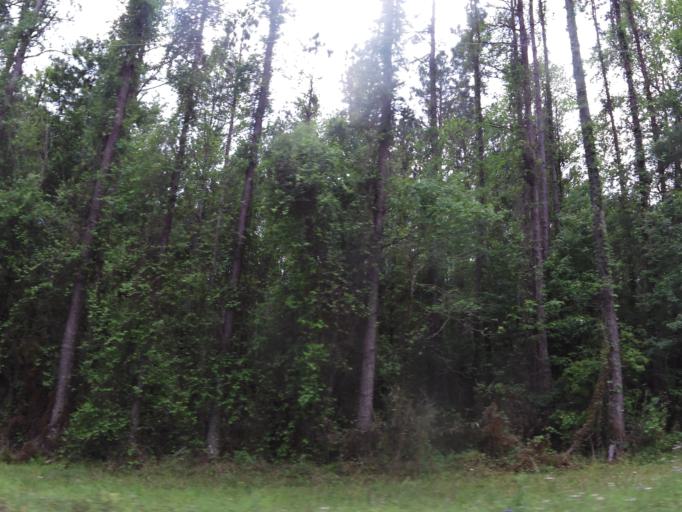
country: US
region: Georgia
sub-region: Charlton County
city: Folkston
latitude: 30.8088
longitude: -82.0618
